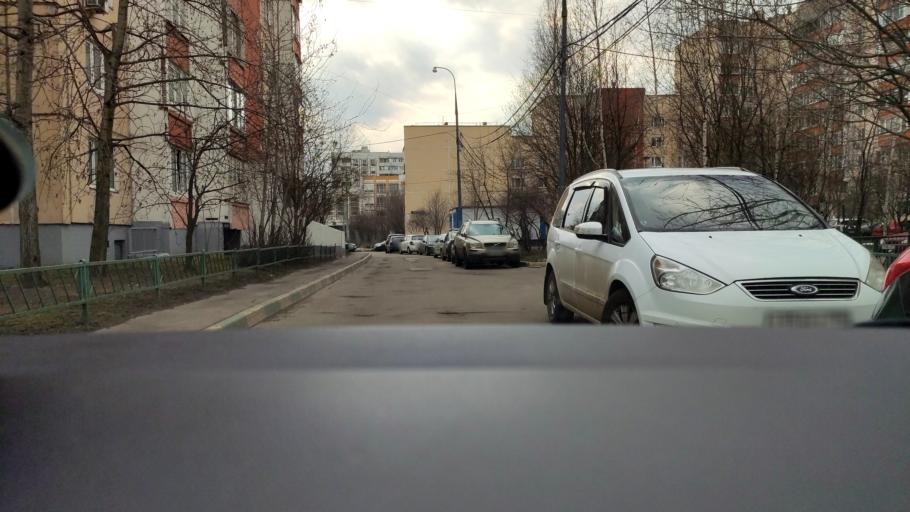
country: RU
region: Moskovskaya
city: Shcherbinka
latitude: 55.5353
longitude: 37.5354
